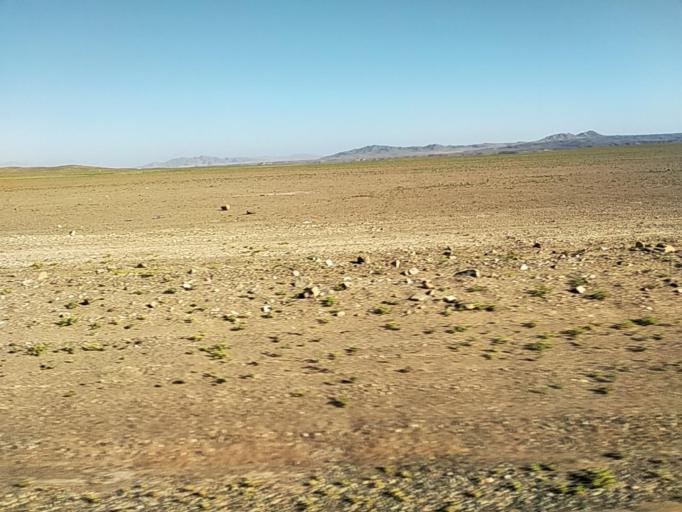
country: CL
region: Atacama
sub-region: Provincia de Copiapo
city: Copiapo
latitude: -27.3203
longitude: -70.7424
